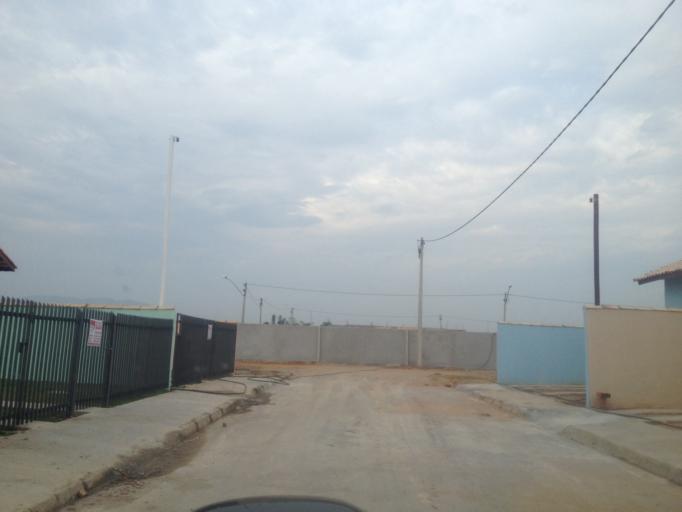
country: BR
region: Rio de Janeiro
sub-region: Porto Real
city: Porto Real
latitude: -22.4208
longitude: -44.3031
